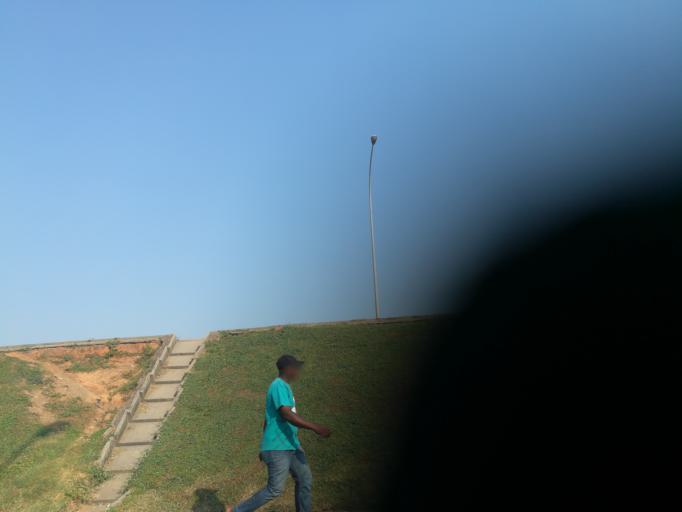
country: NG
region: Abuja Federal Capital Territory
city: Abuja
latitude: 9.0693
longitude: 7.4515
